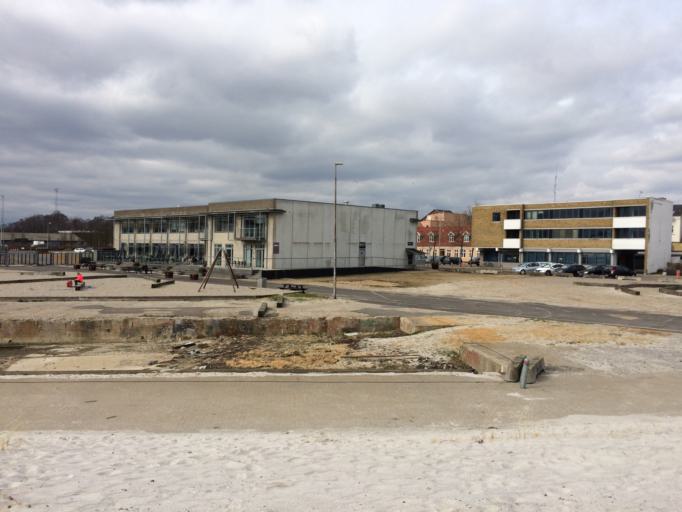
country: DK
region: South Denmark
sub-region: Fredericia Kommune
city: Fredericia
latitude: 55.5602
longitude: 9.7555
